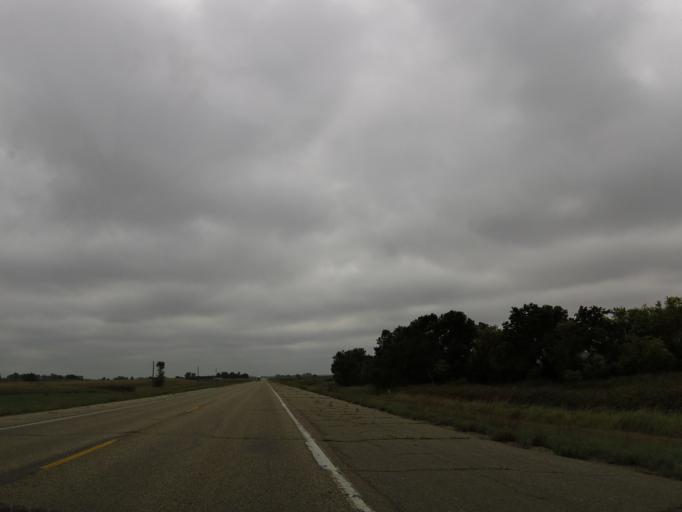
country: US
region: South Dakota
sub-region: Deuel County
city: Clear Lake
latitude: 44.9225
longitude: -96.6795
